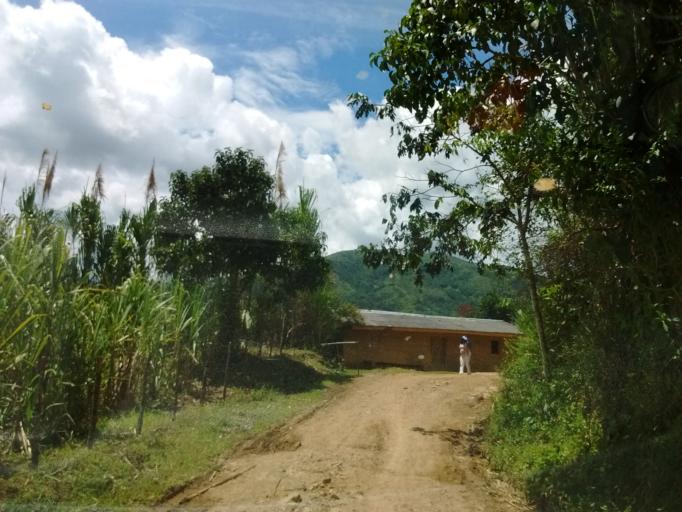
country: CO
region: Cauca
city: Villa Rica
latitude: 2.6568
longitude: -76.7671
